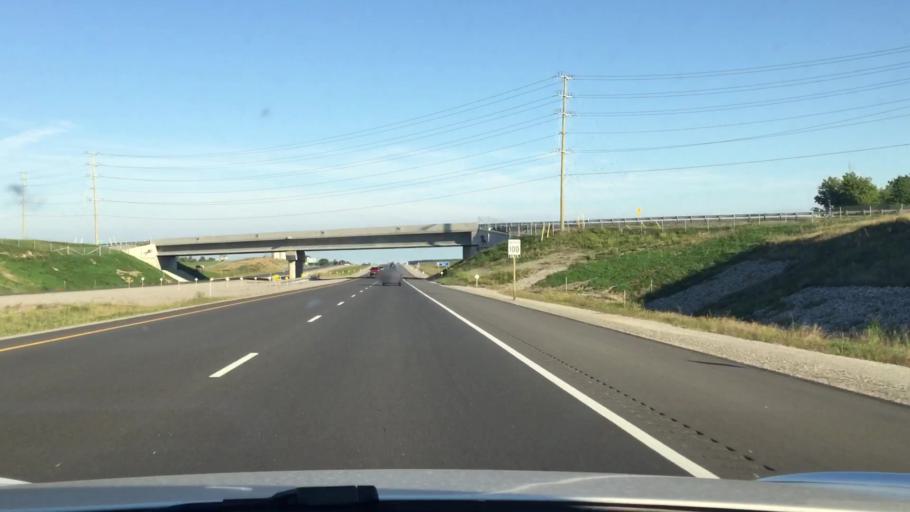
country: CA
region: Ontario
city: Oshawa
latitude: 43.9793
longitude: -78.8567
